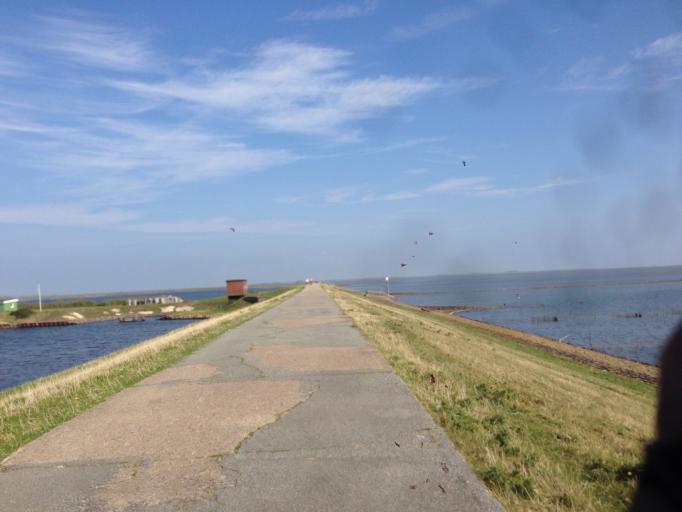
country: DE
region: Schleswig-Holstein
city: Tinnum
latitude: 54.8601
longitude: 8.3111
